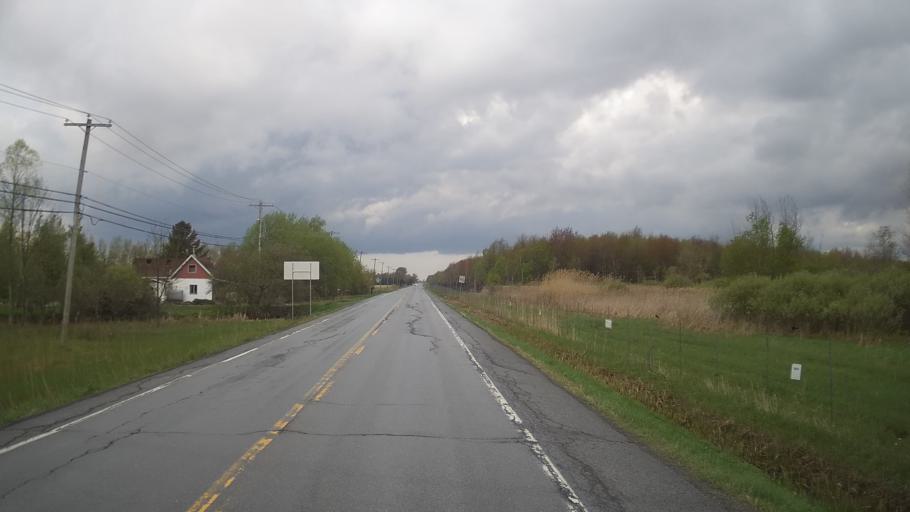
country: CA
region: Quebec
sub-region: Monteregie
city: Farnham
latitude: 45.2941
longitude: -73.0230
